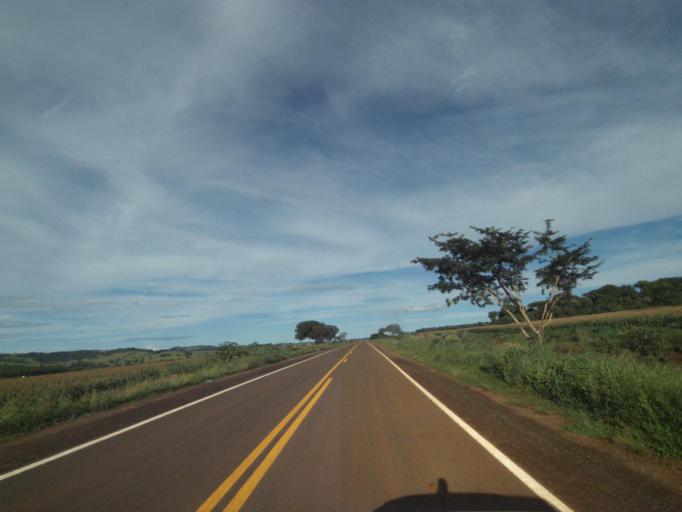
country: BR
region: Goias
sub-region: Jaragua
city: Jaragua
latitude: -15.9063
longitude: -49.5524
